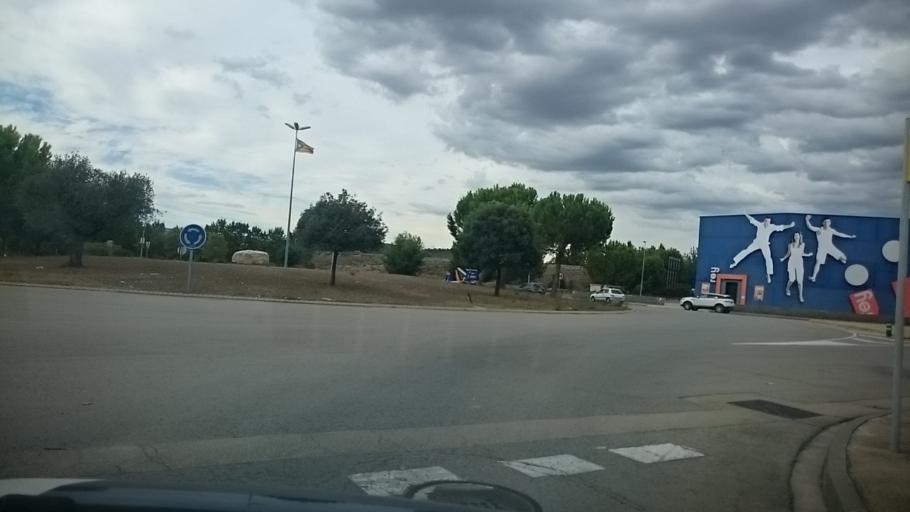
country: ES
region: Catalonia
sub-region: Provincia de Barcelona
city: Vilafranca del Penedes
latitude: 41.3325
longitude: 1.6840
